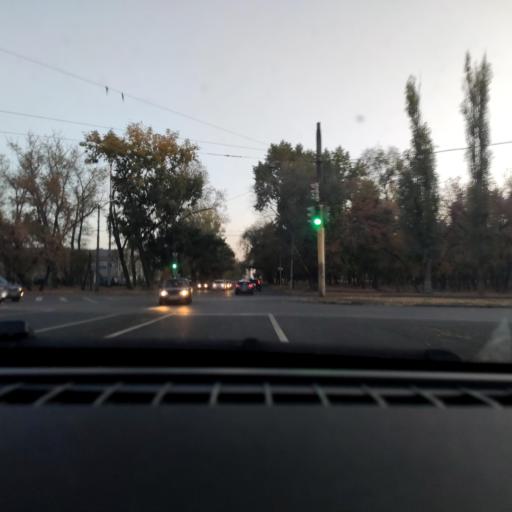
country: RU
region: Voronezj
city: Maslovka
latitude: 51.6006
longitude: 39.2437
